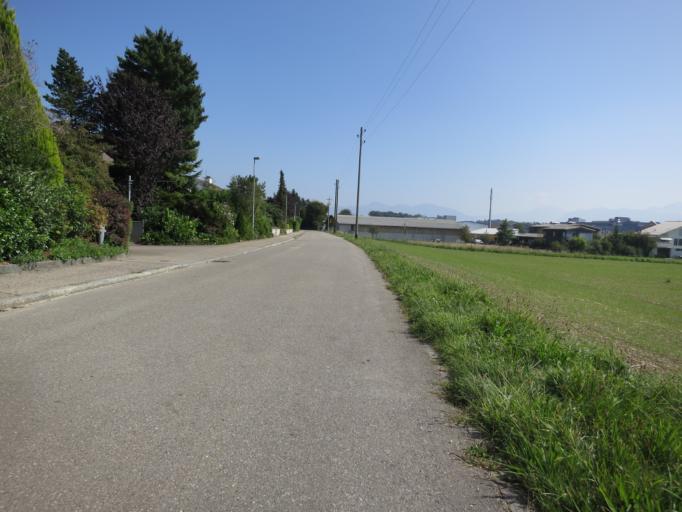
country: CH
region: Zurich
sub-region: Bezirk Hinwil
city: Wolfhausen
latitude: 47.2584
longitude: 8.7922
